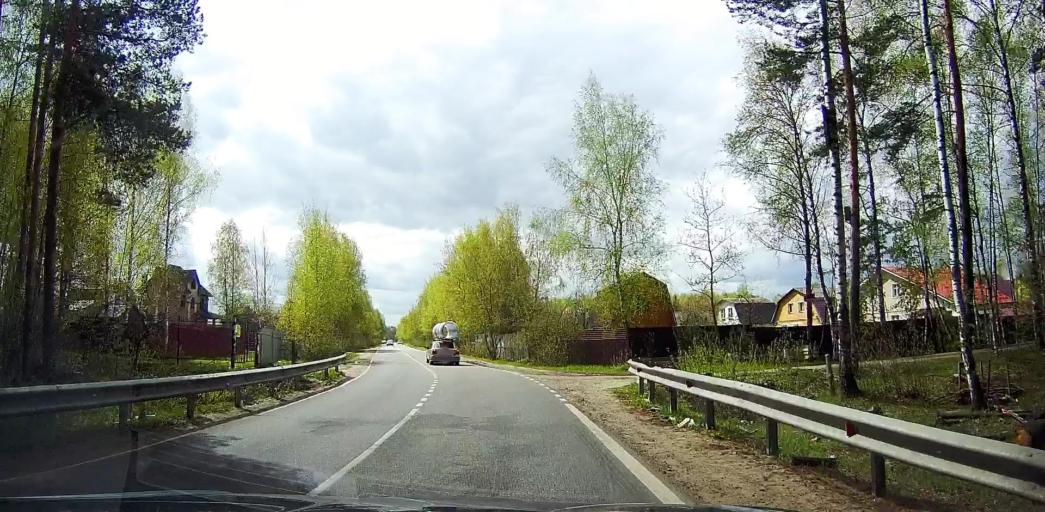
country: RU
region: Moskovskaya
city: Beloozerskiy
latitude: 55.4804
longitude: 38.4226
